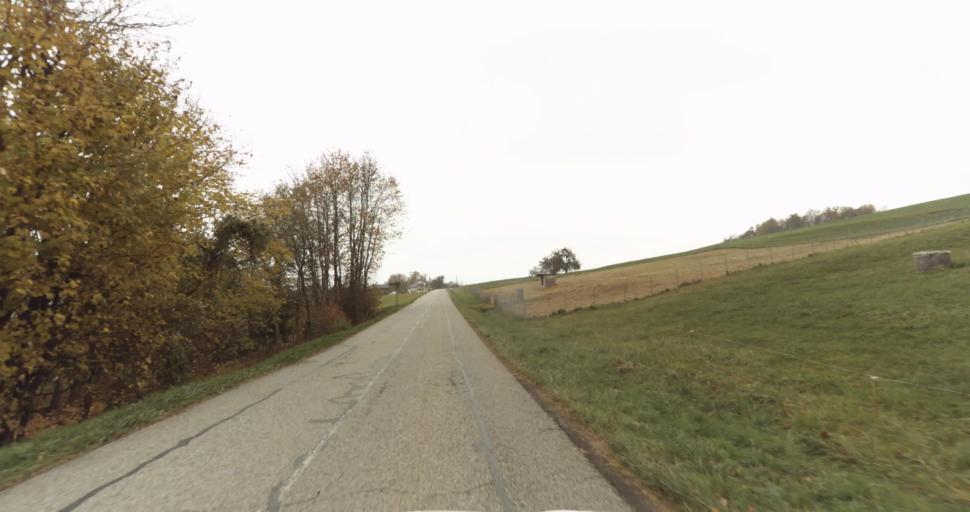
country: FR
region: Rhone-Alpes
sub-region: Departement de la Haute-Savoie
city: Saint-Felix
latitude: 45.7980
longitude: 5.9937
